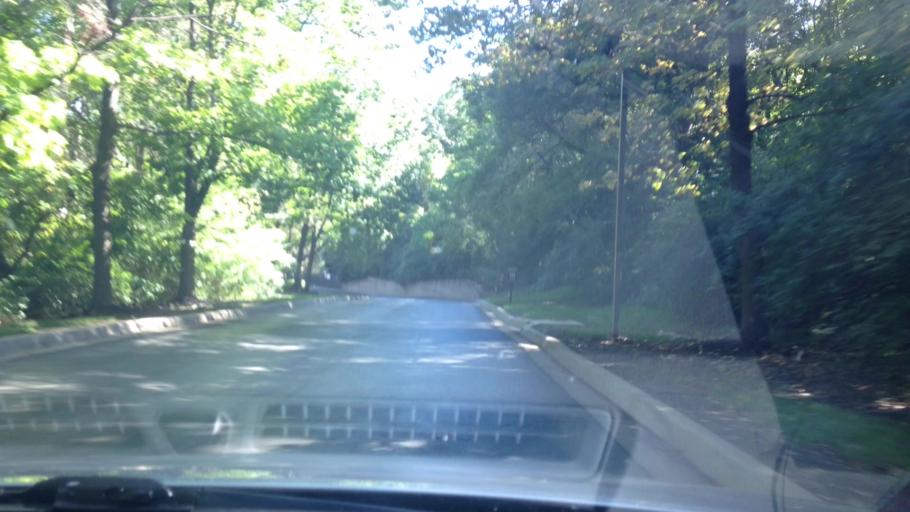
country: US
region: Kansas
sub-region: Johnson County
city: Roeland Park
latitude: 39.0456
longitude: -94.6412
